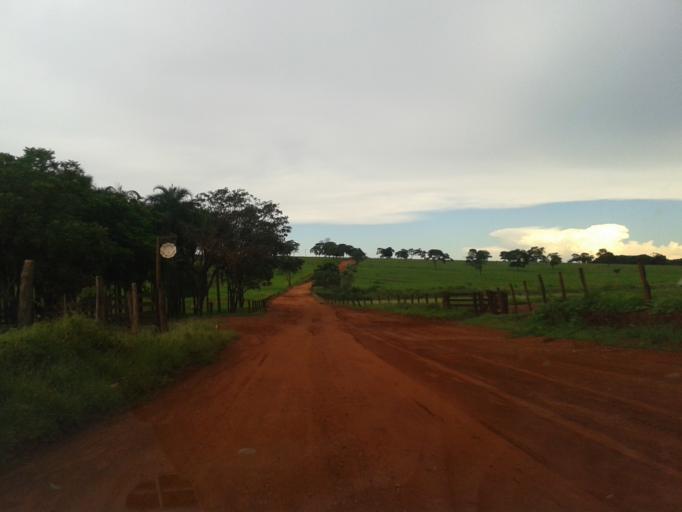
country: BR
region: Minas Gerais
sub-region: Santa Vitoria
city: Santa Vitoria
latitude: -19.1021
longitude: -50.5072
